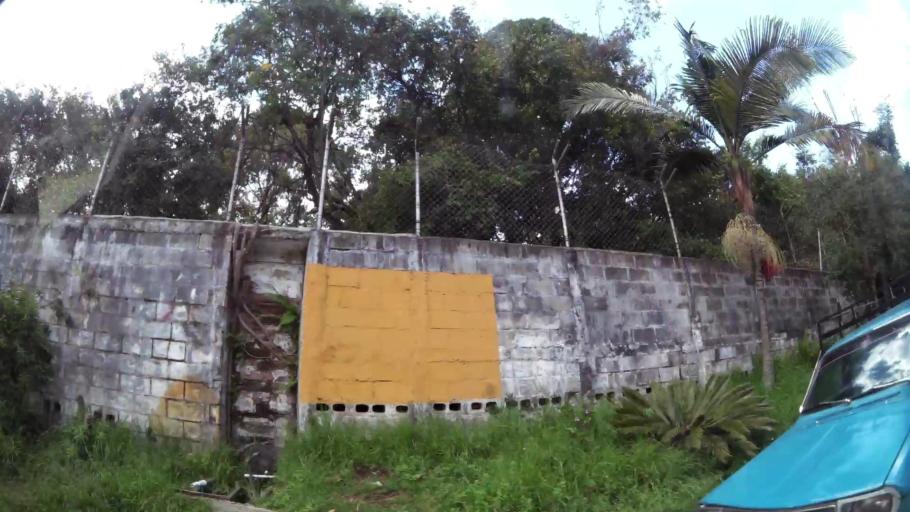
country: CO
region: Antioquia
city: La Estrella
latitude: 6.1606
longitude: -75.6453
